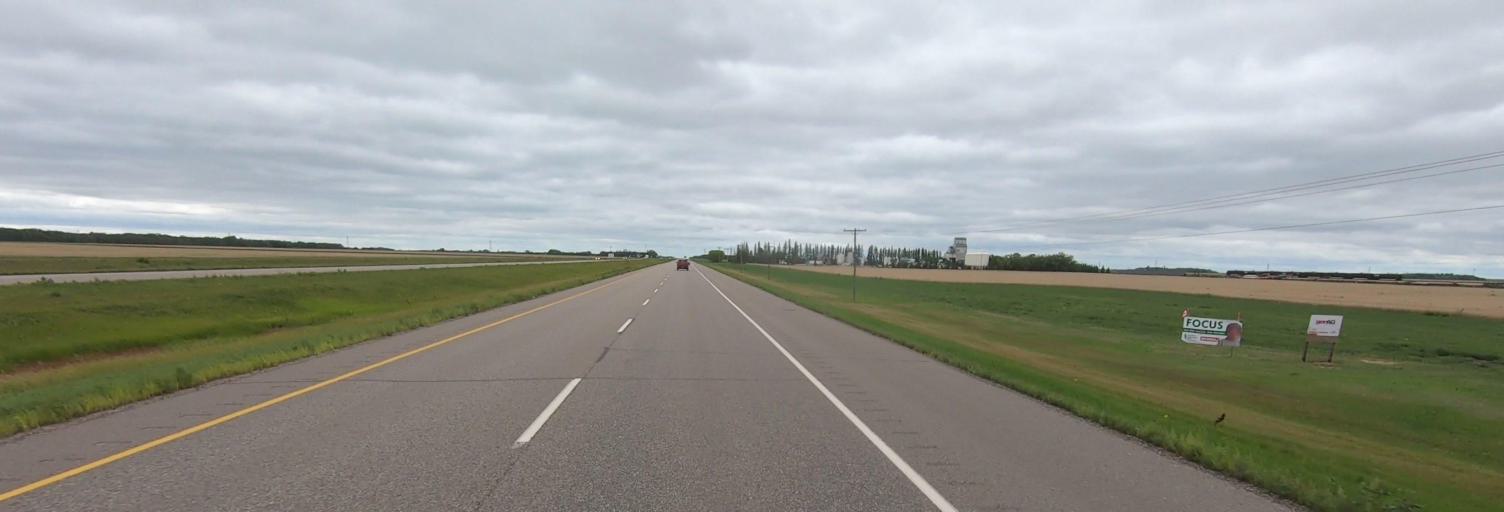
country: CA
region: Manitoba
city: Portage la Prairie
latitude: 49.9752
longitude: -98.5028
